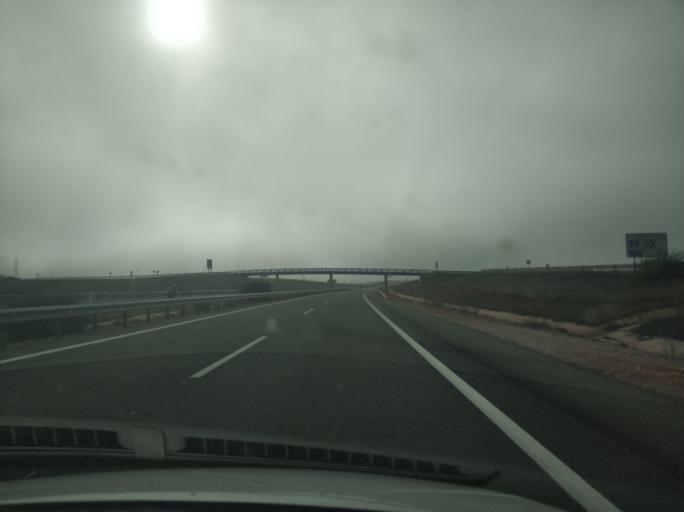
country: ES
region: Castille and Leon
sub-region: Provincia de Soria
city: Alcubilla de las Penas
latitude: 41.2624
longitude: -2.4737
